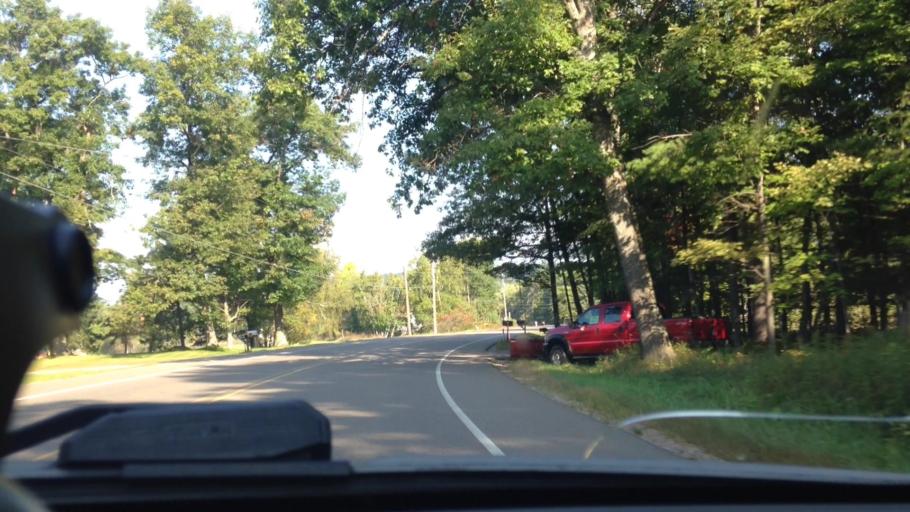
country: US
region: Michigan
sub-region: Dickinson County
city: Quinnesec
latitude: 45.8351
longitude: -88.0086
